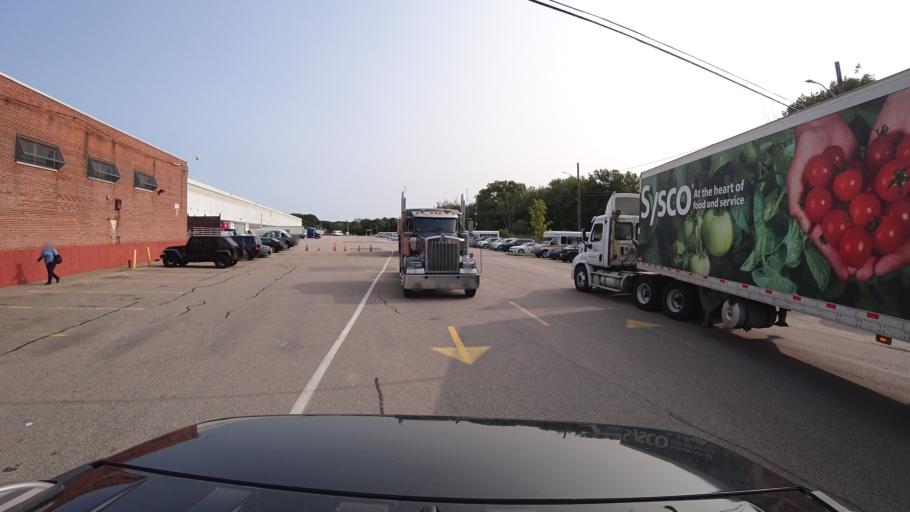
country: US
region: Massachusetts
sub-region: Norfolk County
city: Dedham
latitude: 42.2284
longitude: -71.1336
